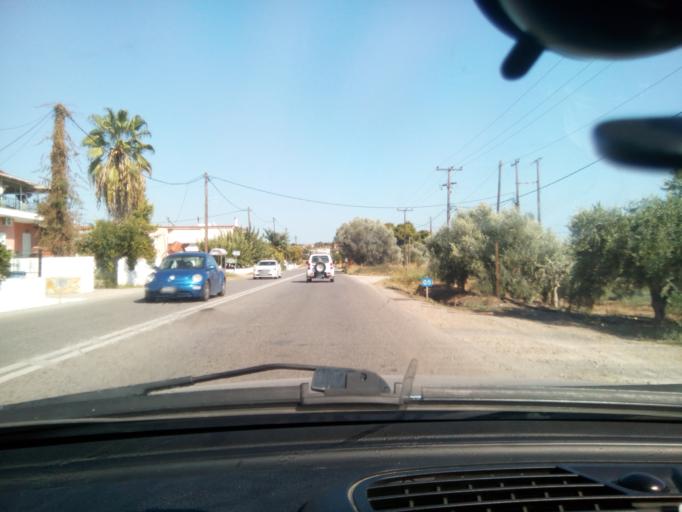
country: GR
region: Central Greece
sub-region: Nomos Evvoias
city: Malakonta
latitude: 38.4051
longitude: 23.7452
